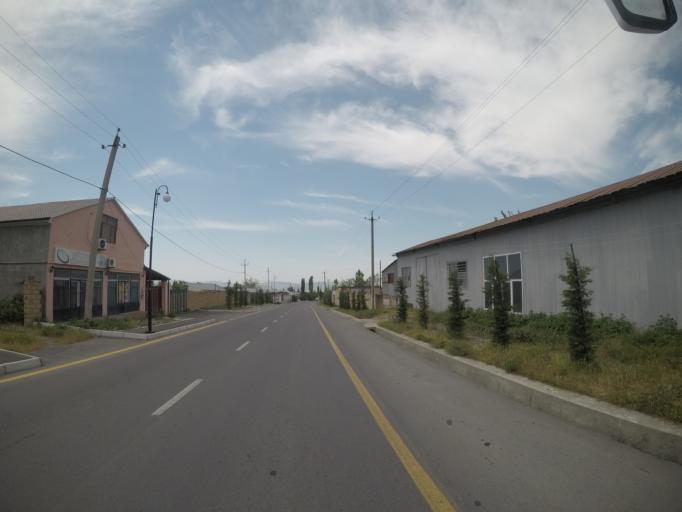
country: AZ
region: Shaki City
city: Sheki
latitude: 41.2138
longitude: 47.1675
